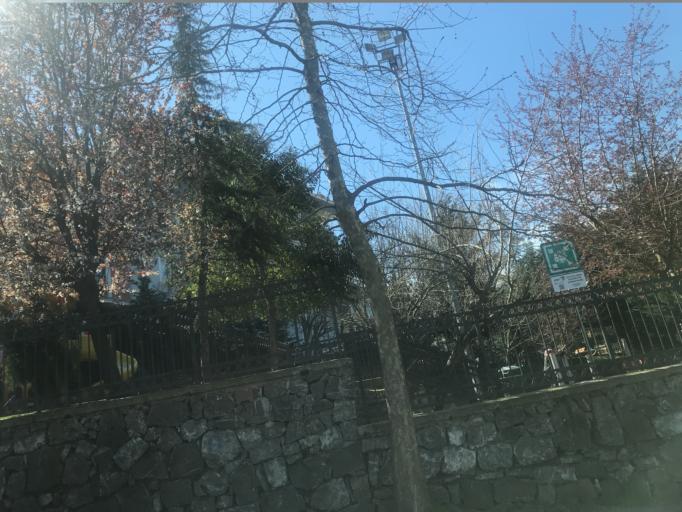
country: TR
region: Istanbul
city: Samandira
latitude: 41.0333
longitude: 29.1809
